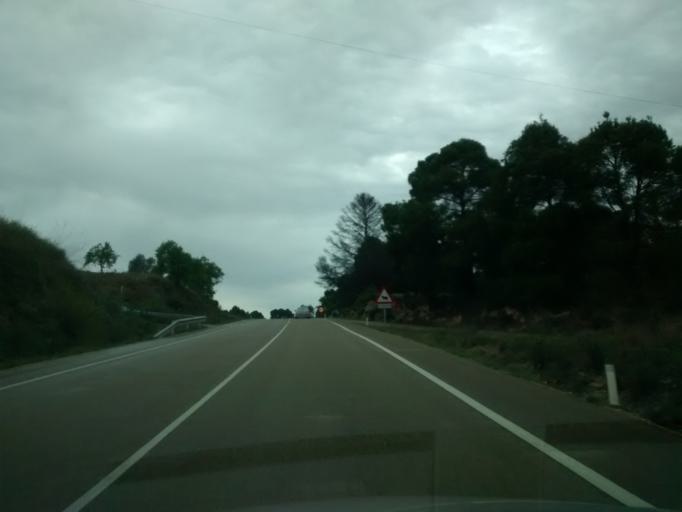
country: ES
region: Aragon
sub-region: Provincia de Zaragoza
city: Caspe
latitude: 41.2125
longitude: 0.0088
